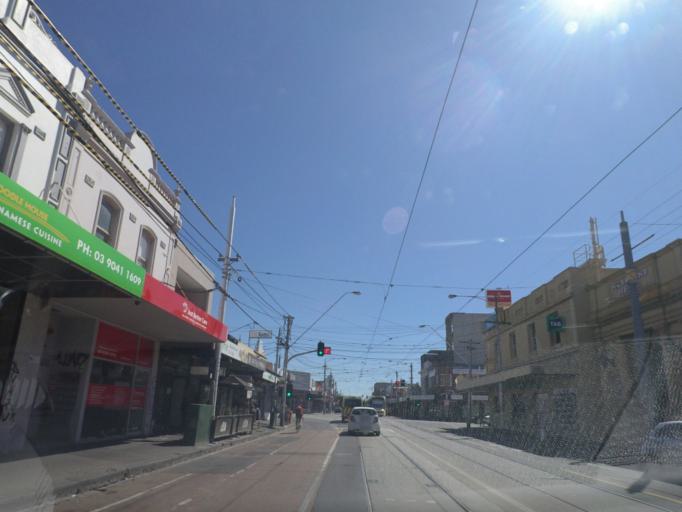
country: AU
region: Victoria
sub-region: Moreland
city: Coburg
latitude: -37.7560
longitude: 144.9641
